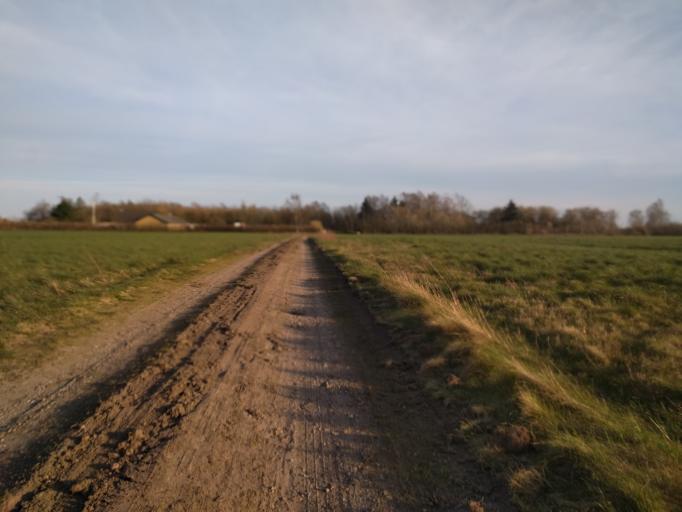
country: DK
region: South Denmark
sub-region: Kerteminde Kommune
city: Langeskov
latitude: 55.3760
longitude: 10.5745
